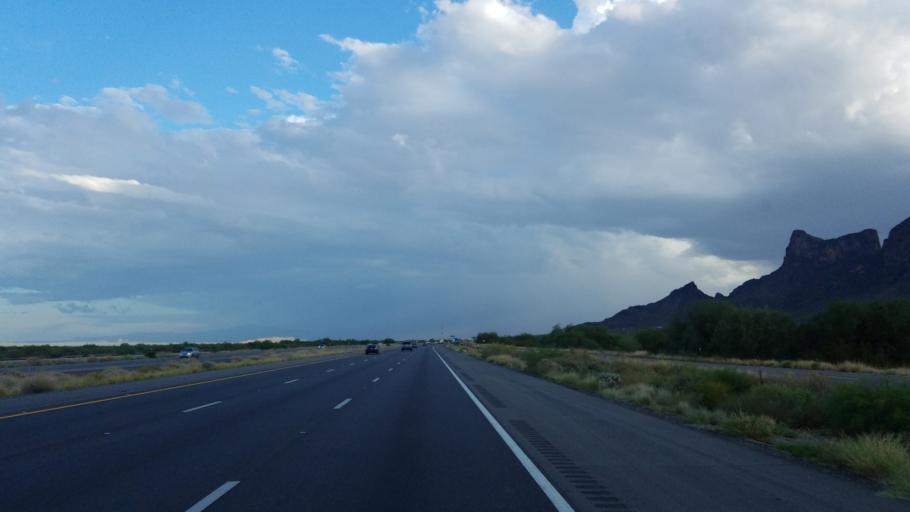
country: US
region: Arizona
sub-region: Pinal County
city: Eloy
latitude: 32.6646
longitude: -111.4174
